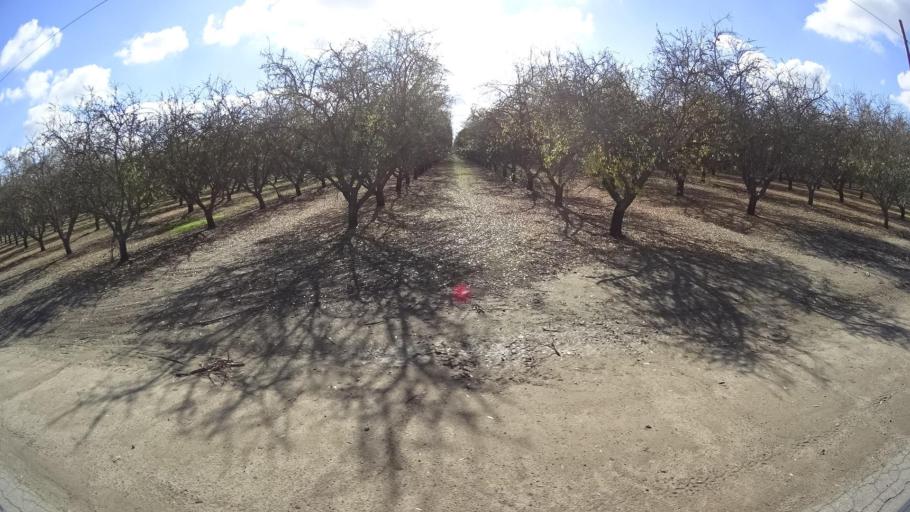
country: US
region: California
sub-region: Kern County
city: McFarland
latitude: 35.6886
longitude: -119.3217
